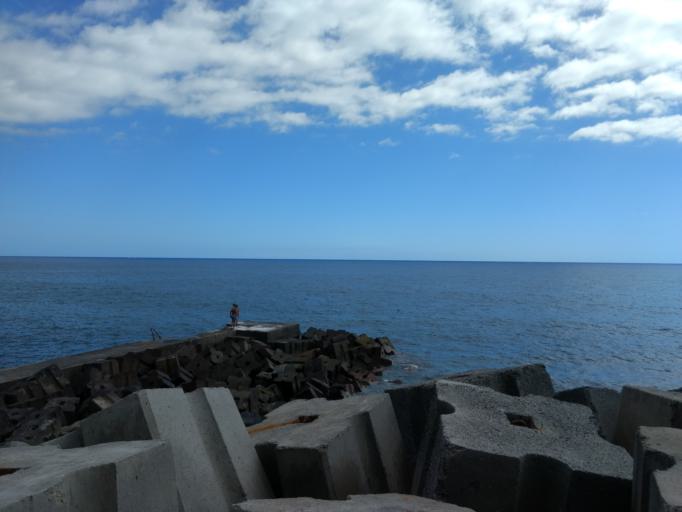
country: PT
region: Madeira
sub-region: Calheta
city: Estreito da Calheta
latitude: 32.7351
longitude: -17.2088
